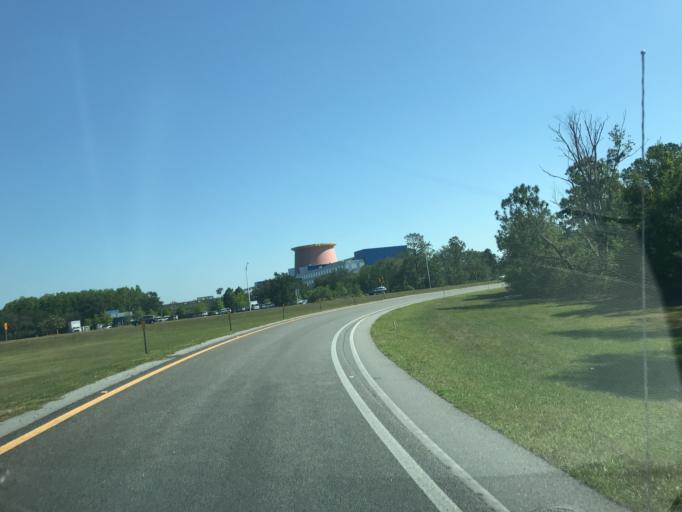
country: US
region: Florida
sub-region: Osceola County
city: Celebration
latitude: 28.3618
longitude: -81.5228
